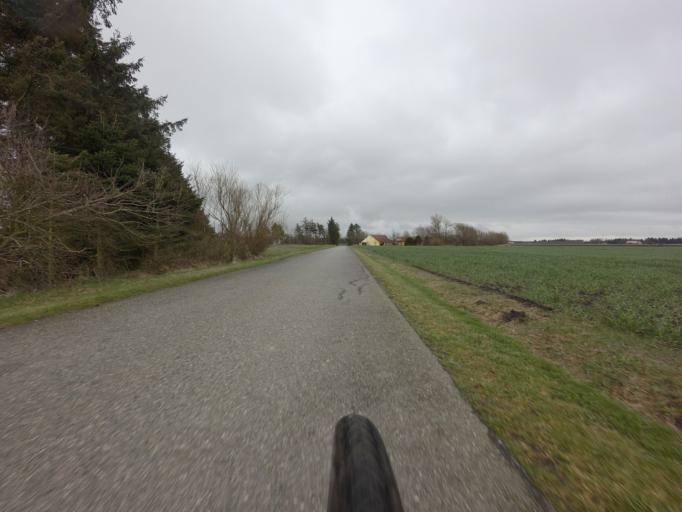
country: DK
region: North Denmark
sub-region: Jammerbugt Kommune
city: Pandrup
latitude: 57.3252
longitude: 9.7862
